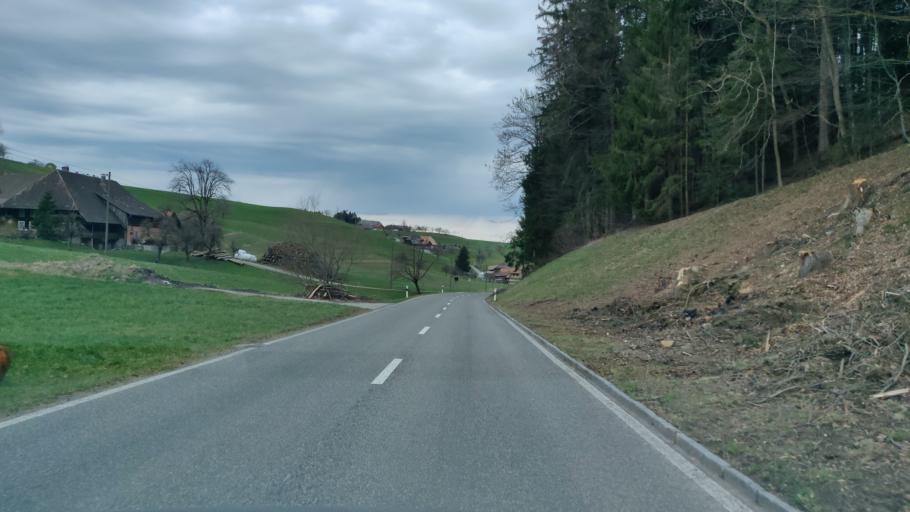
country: CH
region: Bern
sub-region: Emmental District
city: Durrenroth
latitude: 47.1035
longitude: 7.7767
